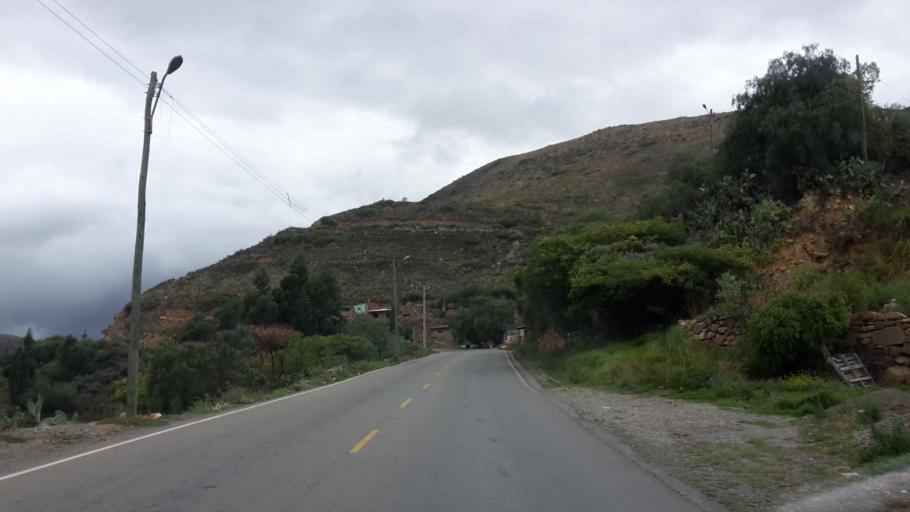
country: BO
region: Cochabamba
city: Punata
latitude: -17.5064
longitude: -65.7992
